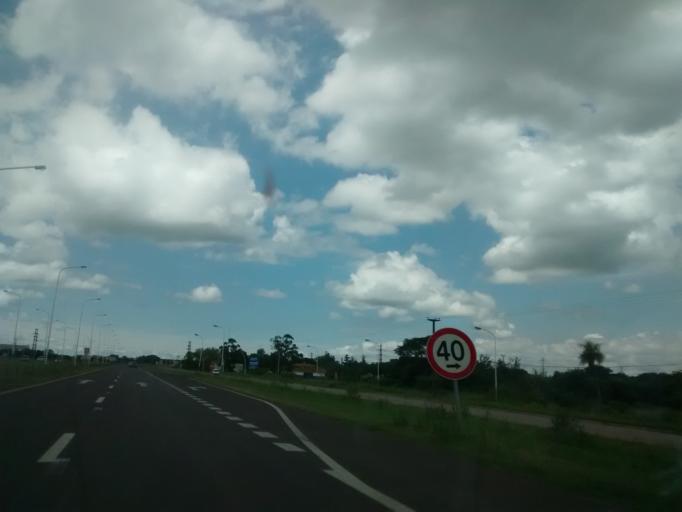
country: AR
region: Chaco
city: Fontana
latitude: -27.4116
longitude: -58.9930
